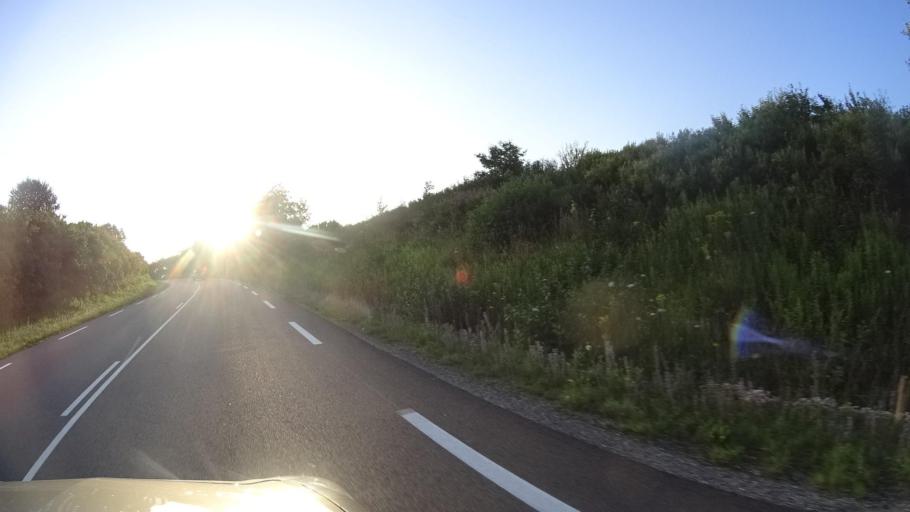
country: FR
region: Franche-Comte
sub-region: Departement du Doubs
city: Doubs
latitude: 46.9125
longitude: 6.2812
